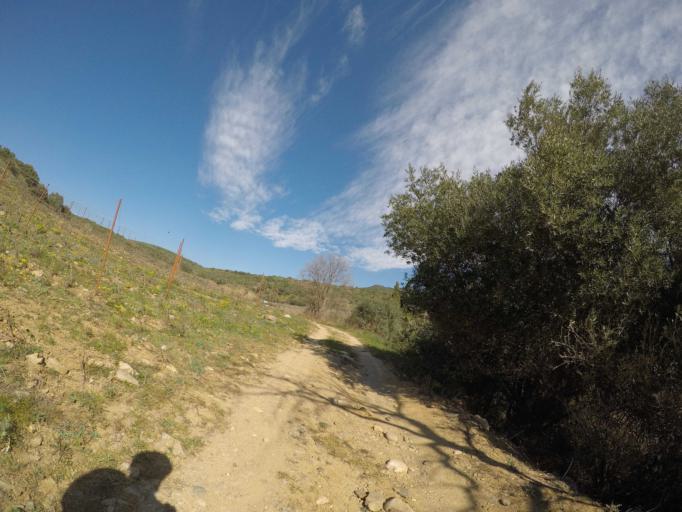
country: FR
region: Languedoc-Roussillon
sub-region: Departement des Pyrenees-Orientales
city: Millas
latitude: 42.7127
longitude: 2.6967
